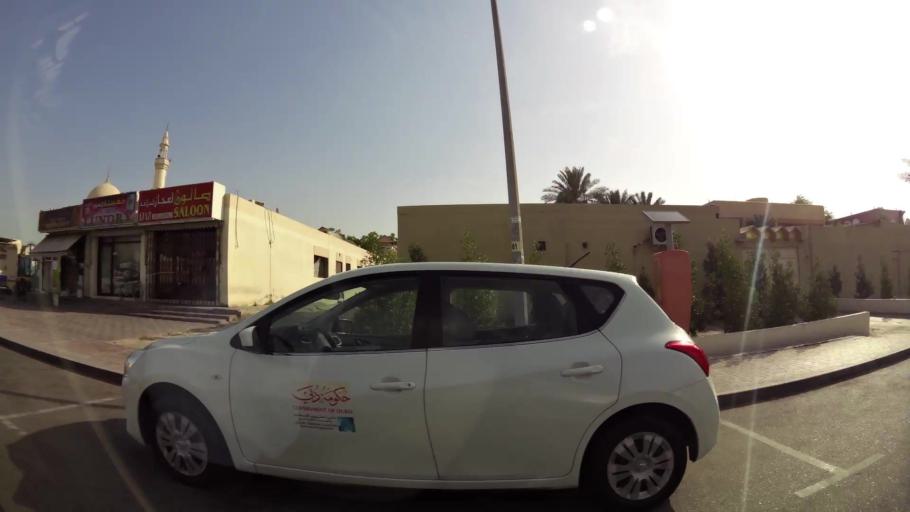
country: AE
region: Ash Shariqah
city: Sharjah
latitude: 25.2274
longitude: 55.3810
